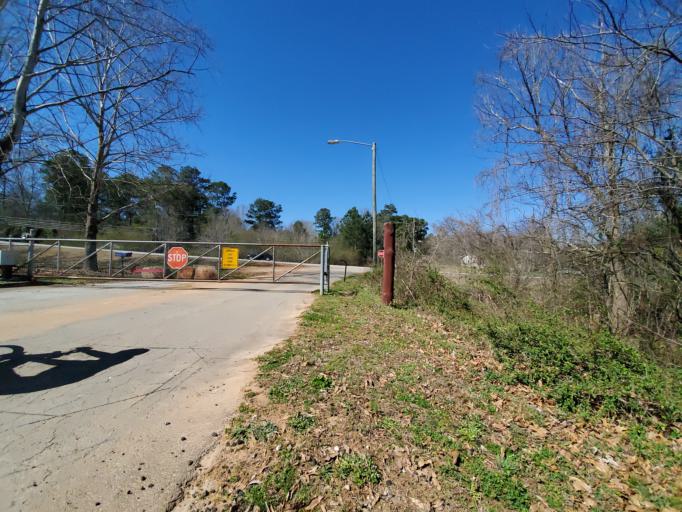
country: US
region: Georgia
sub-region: Barrow County
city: Winder
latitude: 33.9846
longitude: -83.7333
